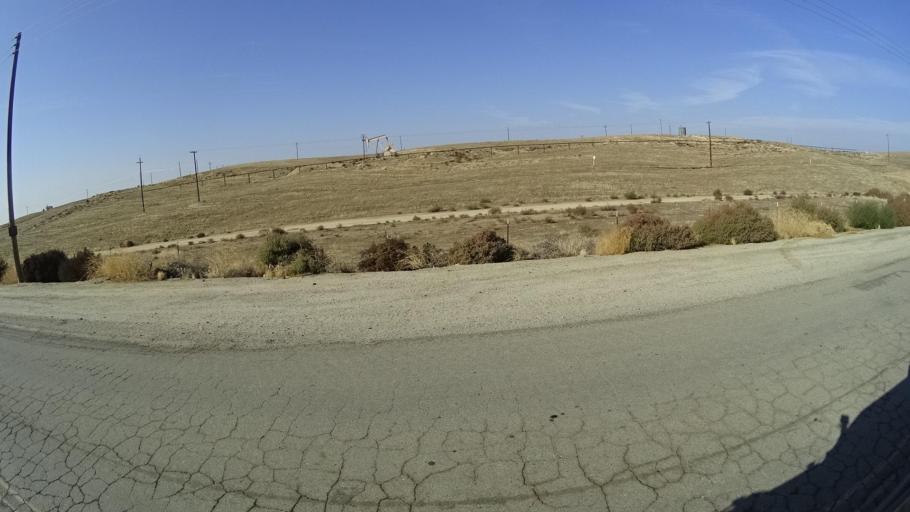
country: US
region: California
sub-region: Kern County
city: Oildale
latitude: 35.4817
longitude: -119.0460
